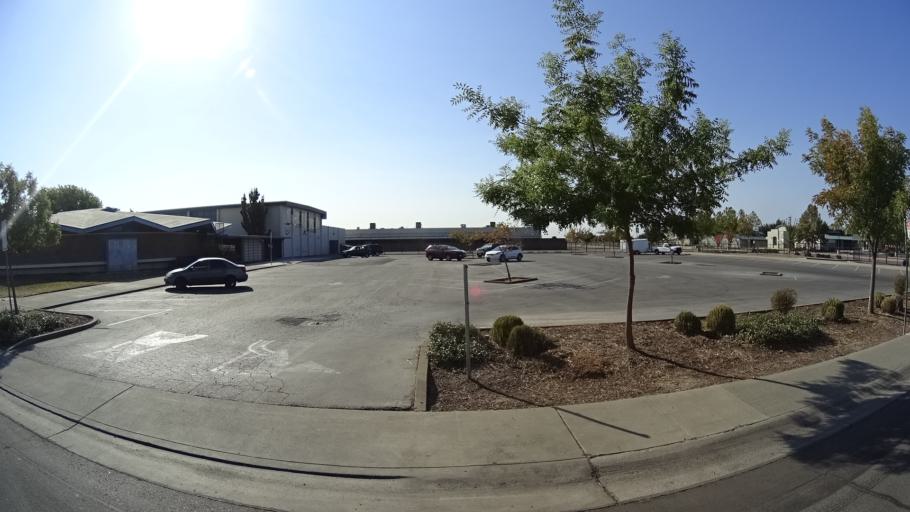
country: US
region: California
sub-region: Sacramento County
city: Parkway
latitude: 38.4772
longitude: -121.4853
